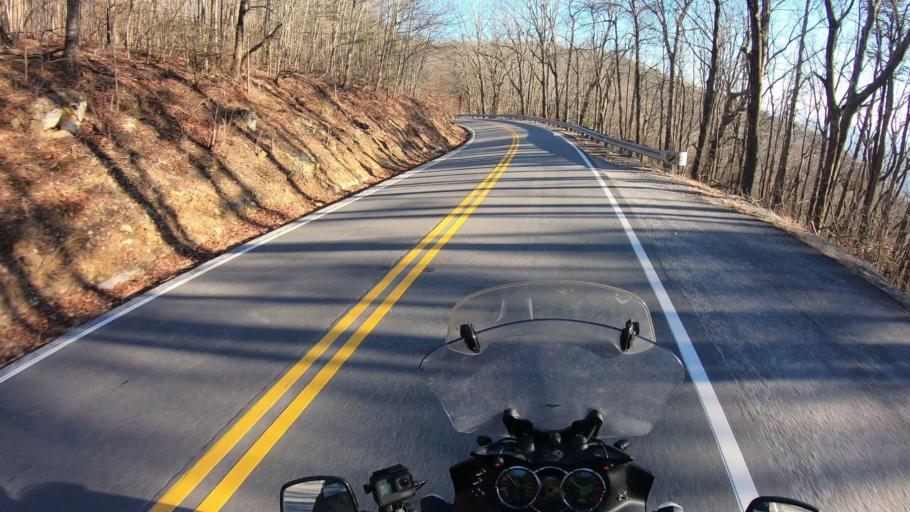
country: US
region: Georgia
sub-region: Lumpkin County
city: Dahlonega
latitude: 34.6692
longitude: -83.9914
